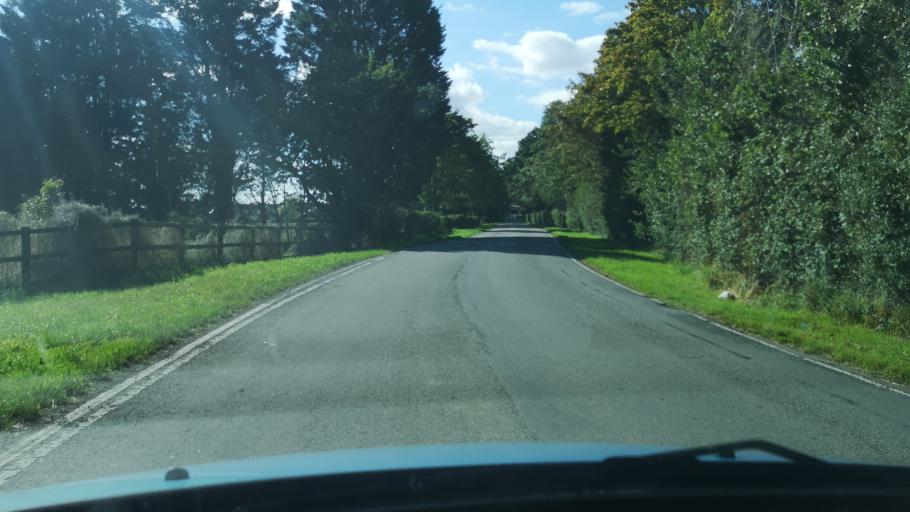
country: GB
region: England
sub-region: North Lincolnshire
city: Eastoft
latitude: 53.6360
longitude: -0.7784
